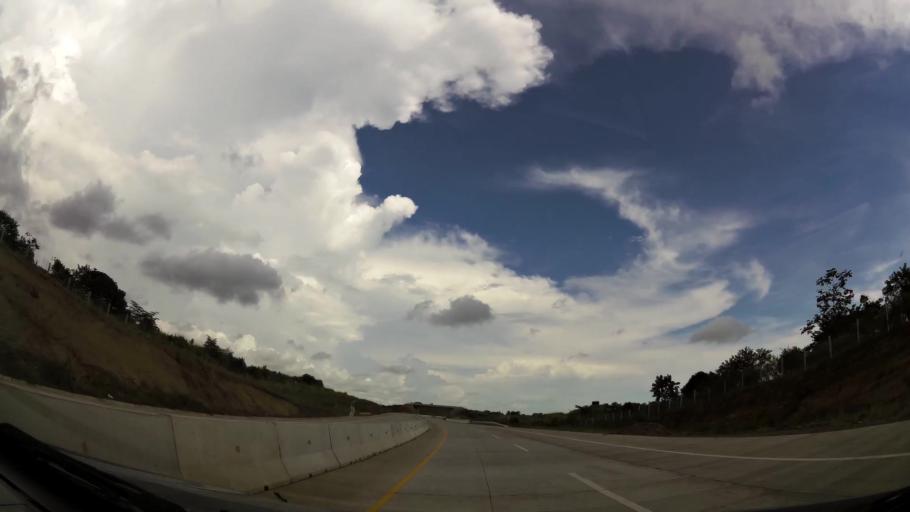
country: PA
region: Panama
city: Tocumen
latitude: 9.1051
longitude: -79.3981
